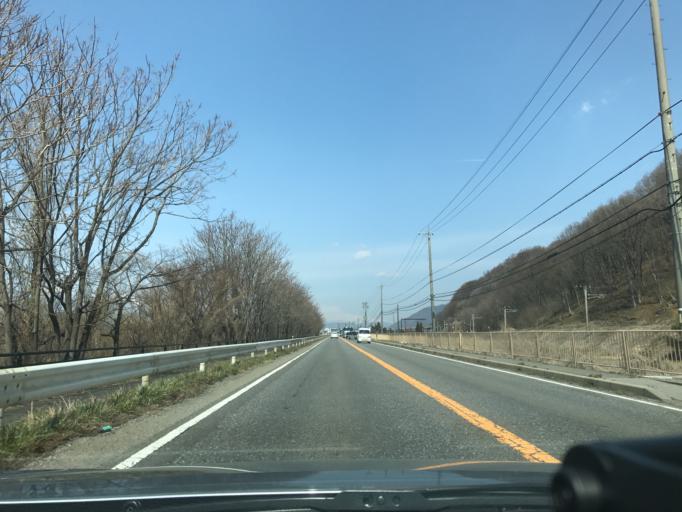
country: JP
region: Nagano
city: Matsumoto
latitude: 36.2584
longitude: 137.9489
